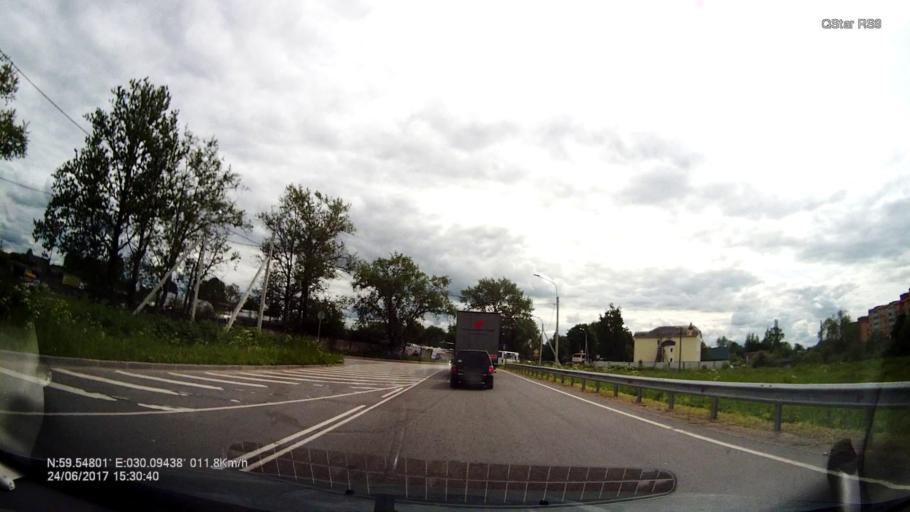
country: RU
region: Leningrad
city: Mariyenburg
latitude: 59.5479
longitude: 30.0944
